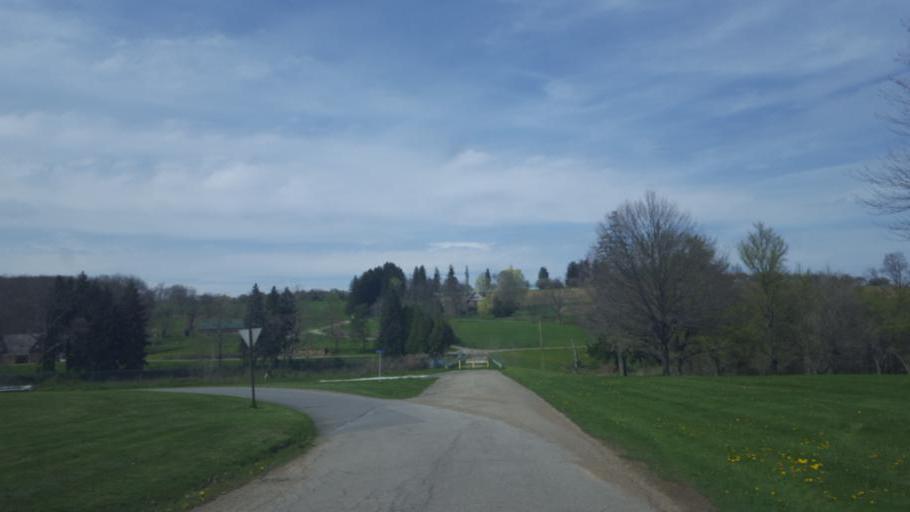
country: US
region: Pennsylvania
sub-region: Venango County
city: Sugarcreek
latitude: 41.3741
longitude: -79.9286
